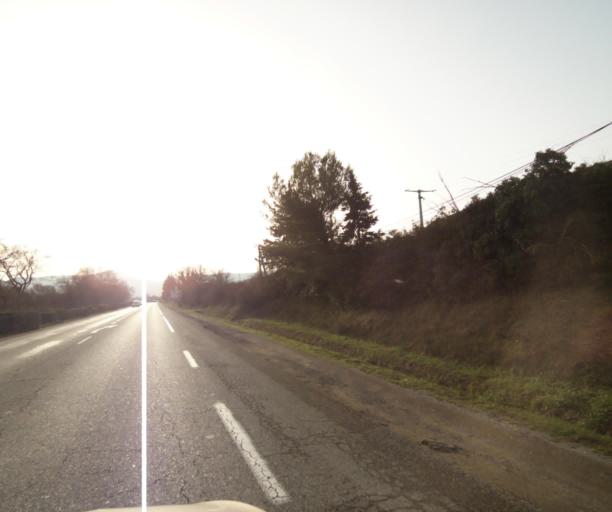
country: FR
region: Provence-Alpes-Cote d'Azur
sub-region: Departement des Bouches-du-Rhone
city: Trets
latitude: 43.4538
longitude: 5.6677
